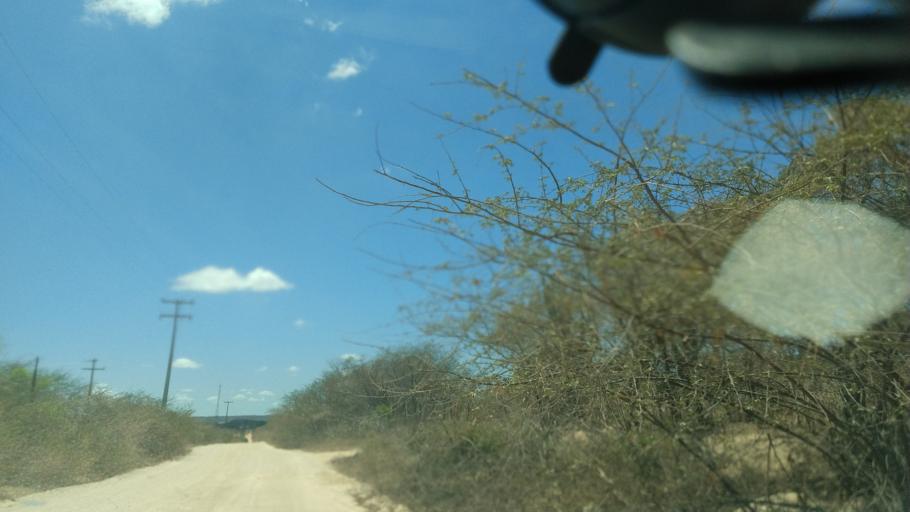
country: BR
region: Rio Grande do Norte
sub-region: Cerro Cora
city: Cerro Cora
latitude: -6.0273
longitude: -36.3374
